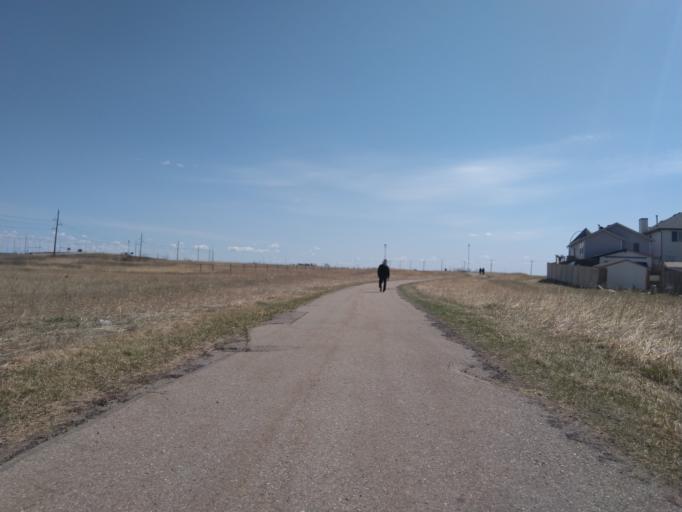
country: CA
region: Alberta
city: Chestermere
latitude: 51.0946
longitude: -113.9301
